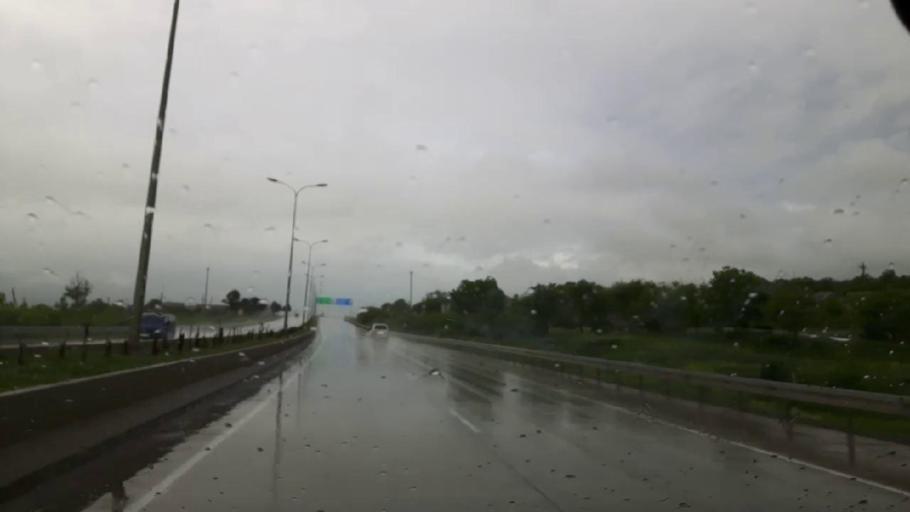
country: GE
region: Shida Kartli
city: Gori
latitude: 42.0270
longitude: 44.1953
